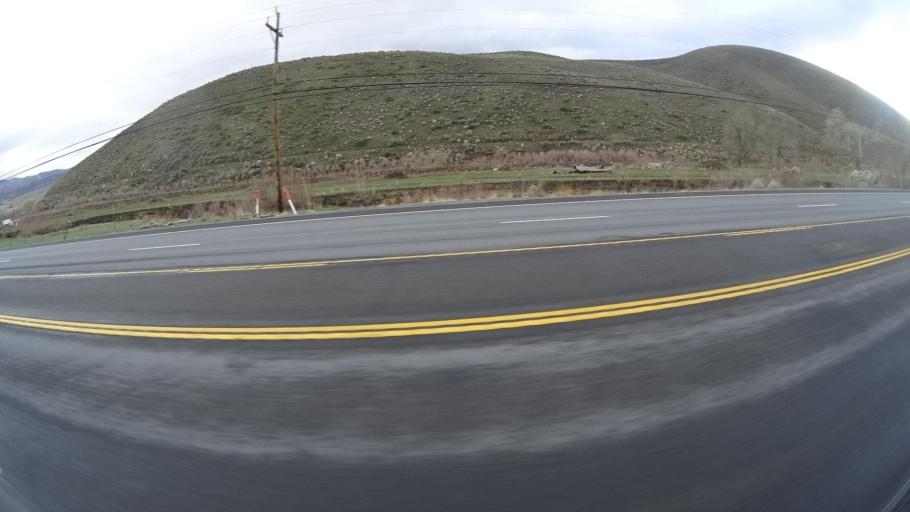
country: US
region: Nevada
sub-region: Storey County
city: Virginia City
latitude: 39.3628
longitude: -119.7580
